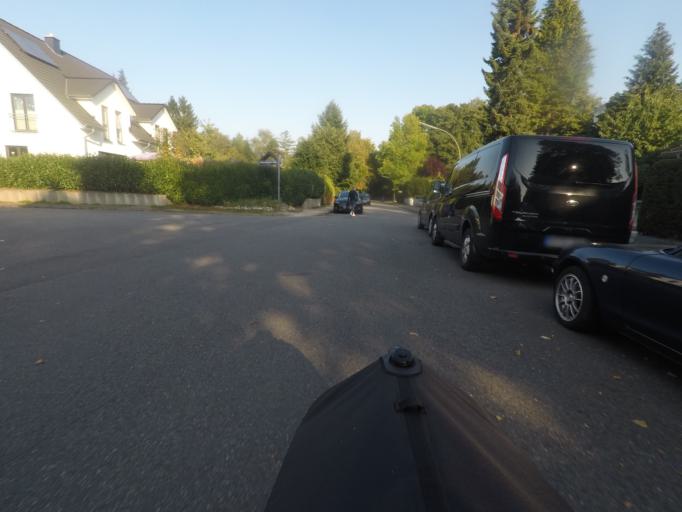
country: DE
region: Hamburg
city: Farmsen-Berne
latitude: 53.6129
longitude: 10.1609
